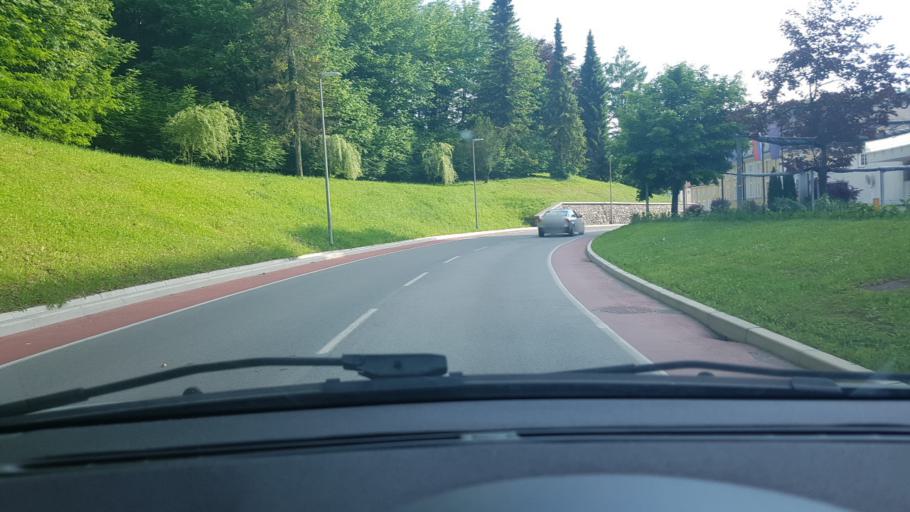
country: SI
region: Rogaska Slatina
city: Rogaska Slatina
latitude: 46.2380
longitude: 15.6419
